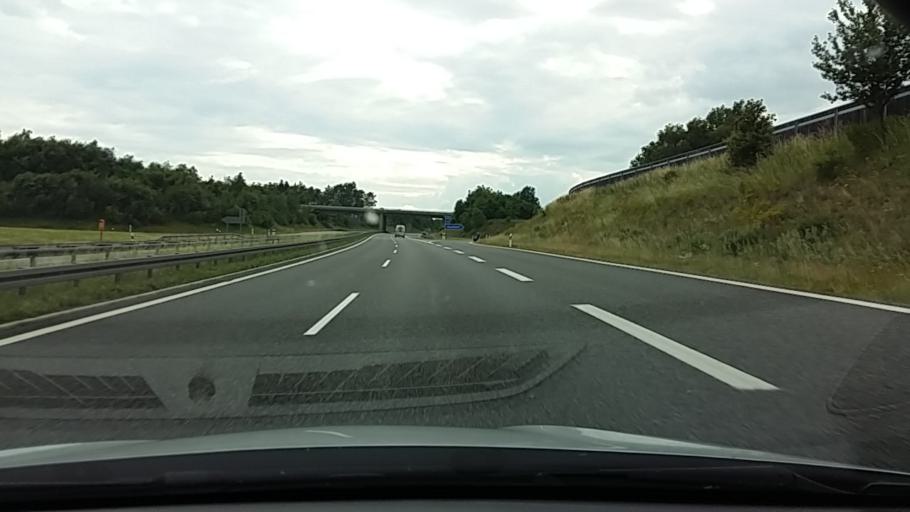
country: DE
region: Bavaria
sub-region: Upper Palatinate
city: Vohenstrauss
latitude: 49.6178
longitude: 12.3550
